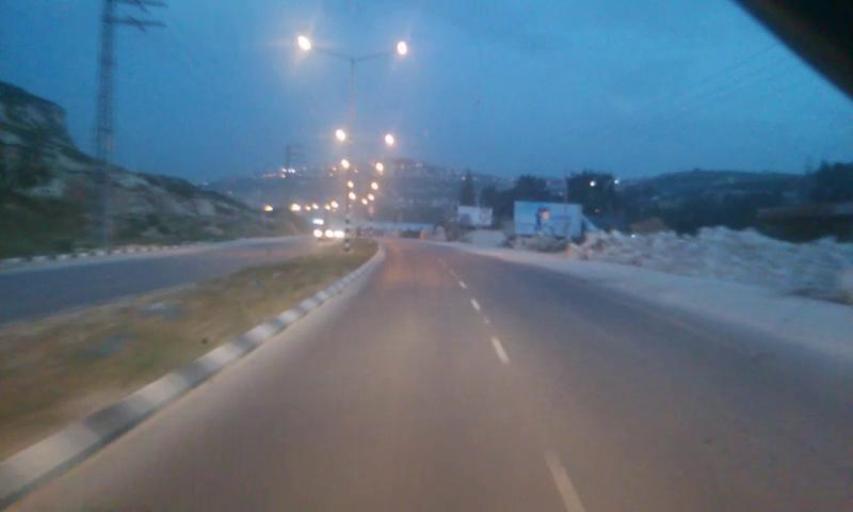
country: PS
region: West Bank
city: Dayr Sharaf
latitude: 32.2452
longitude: 35.1944
